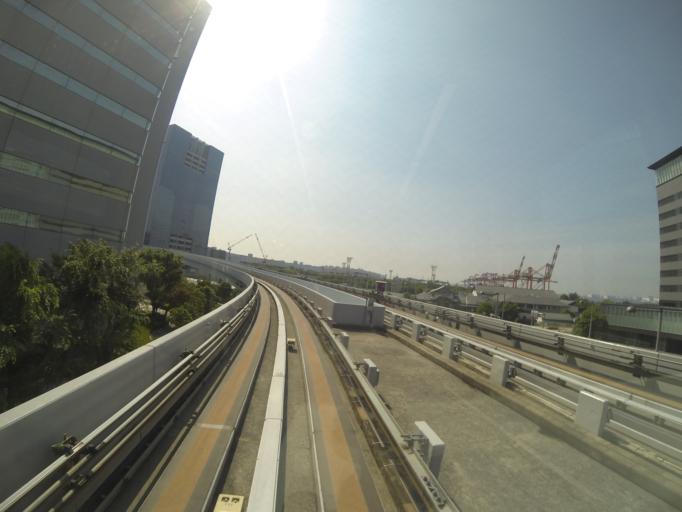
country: JP
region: Tokyo
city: Tokyo
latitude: 35.6174
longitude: 139.7764
